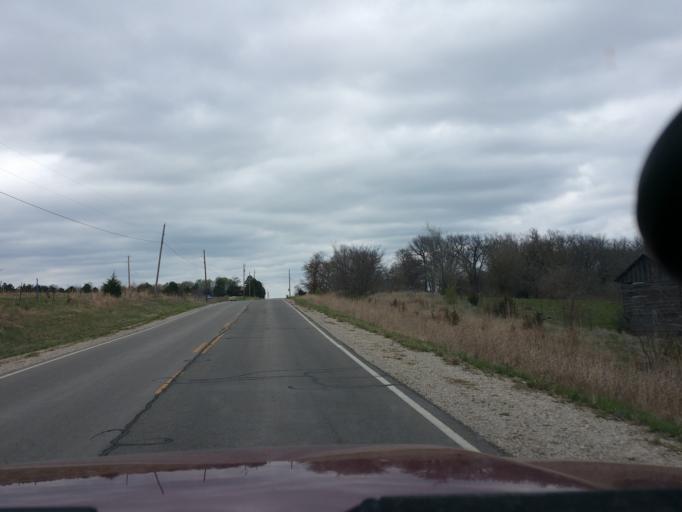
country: US
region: Missouri
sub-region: Cass County
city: Belton
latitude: 38.8170
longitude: -94.6118
